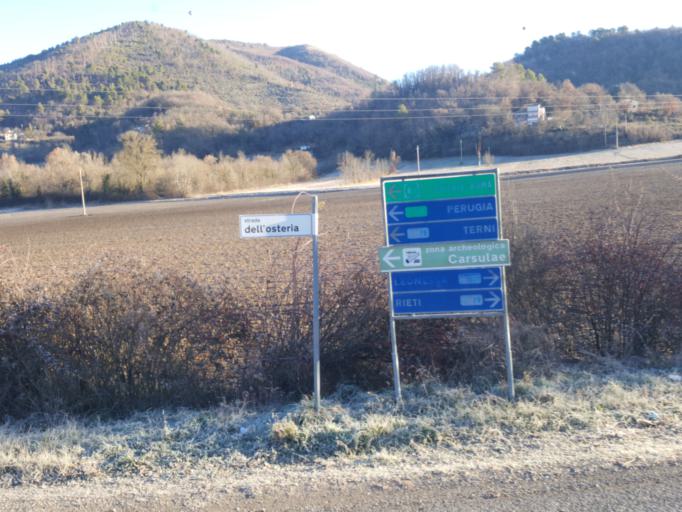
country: IT
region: Latium
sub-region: Provincia di Rieti
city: Labro
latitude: 42.5359
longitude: 12.7744
